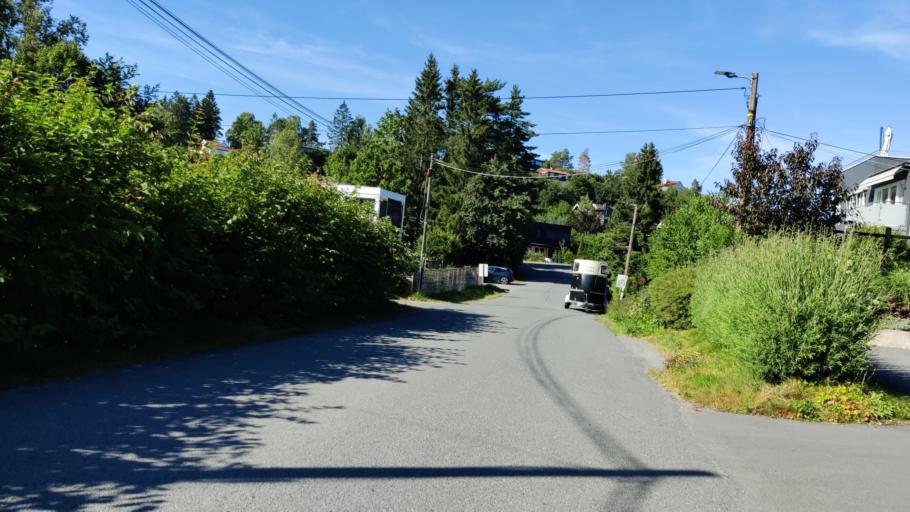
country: NO
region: Akershus
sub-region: Baerum
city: Lysaker
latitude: 59.9271
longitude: 10.6001
